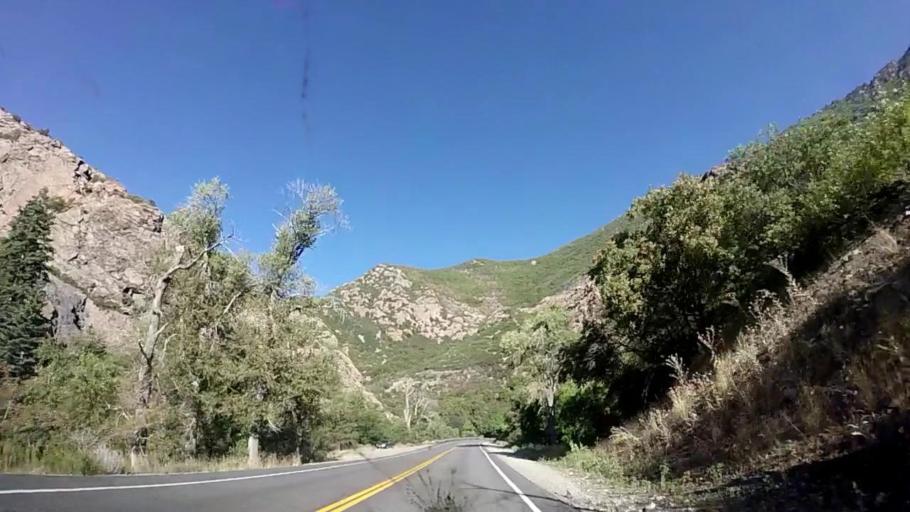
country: US
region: Utah
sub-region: Salt Lake County
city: Cottonwood Heights
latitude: 40.6239
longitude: -111.7638
